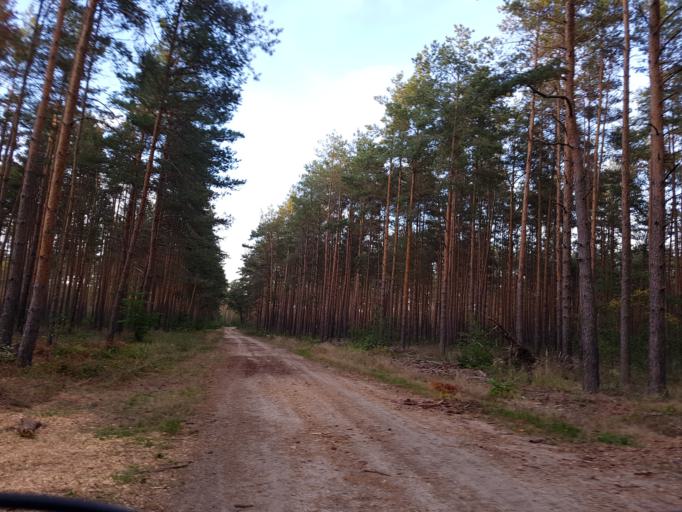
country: DE
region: Brandenburg
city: Trobitz
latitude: 51.5556
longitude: 13.4496
